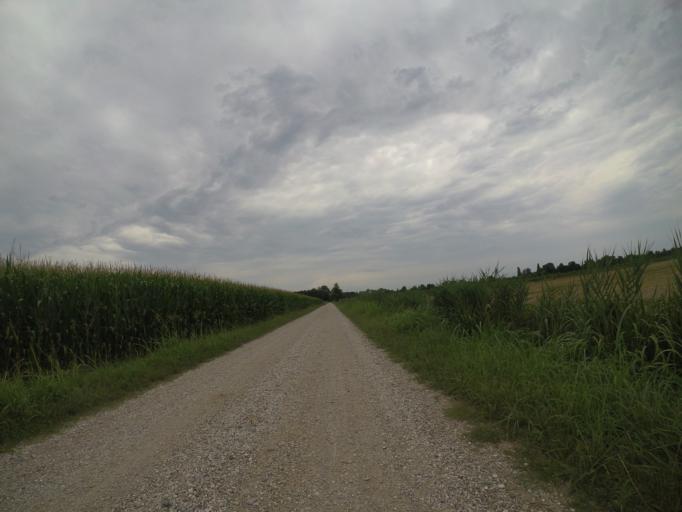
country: IT
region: Friuli Venezia Giulia
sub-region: Provincia di Udine
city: Rivignano
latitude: 45.9034
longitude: 13.0620
